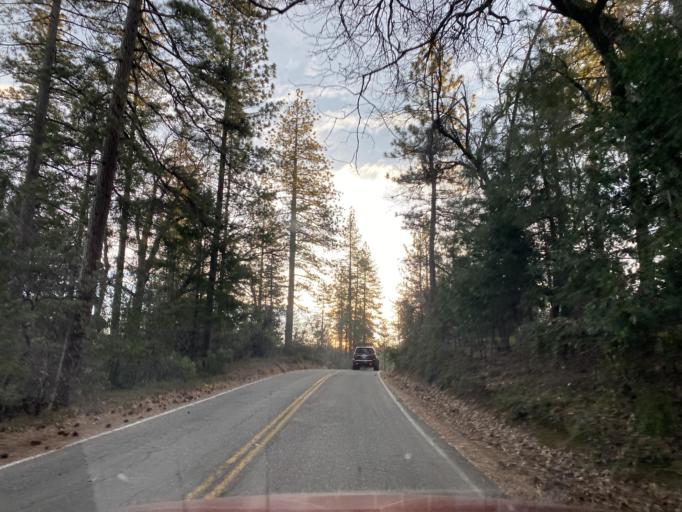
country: US
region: California
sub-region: Amador County
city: Pioneer
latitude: 38.4991
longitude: -120.6082
